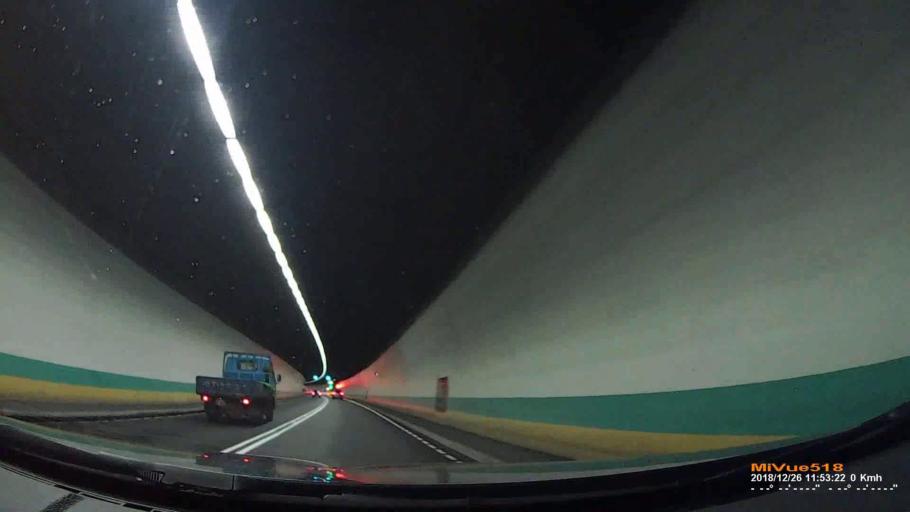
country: TW
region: Taiwan
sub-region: Keelung
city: Keelung
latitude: 24.9591
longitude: 121.6919
